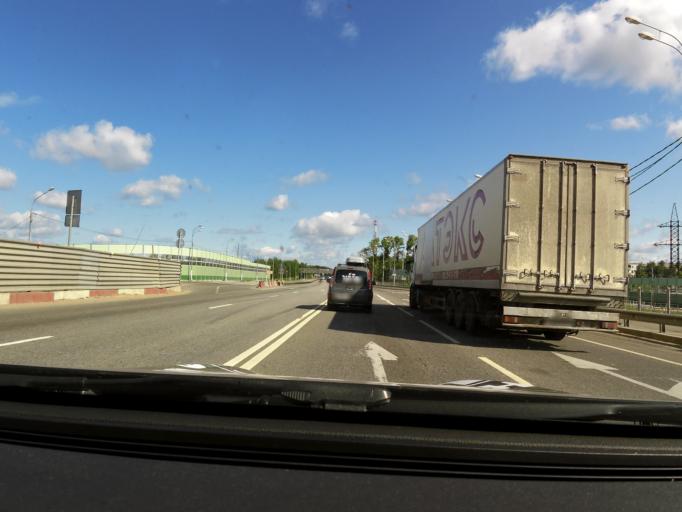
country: RU
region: Tverskaya
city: Tver
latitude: 56.8515
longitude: 35.7907
